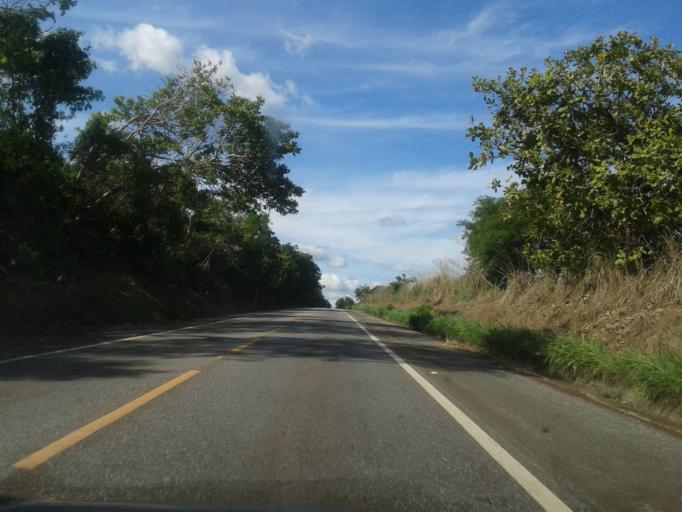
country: BR
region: Goias
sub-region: Mozarlandia
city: Mozarlandia
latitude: -14.9553
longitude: -50.5790
